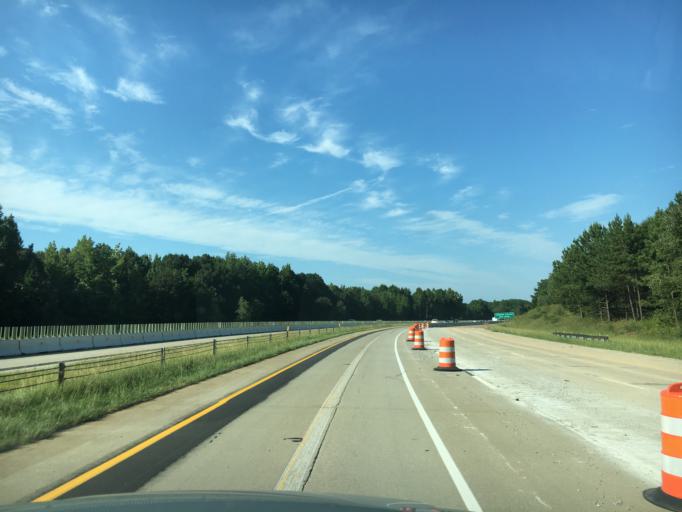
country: US
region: South Carolina
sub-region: Spartanburg County
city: Southern Shops
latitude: 34.9883
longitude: -82.0009
